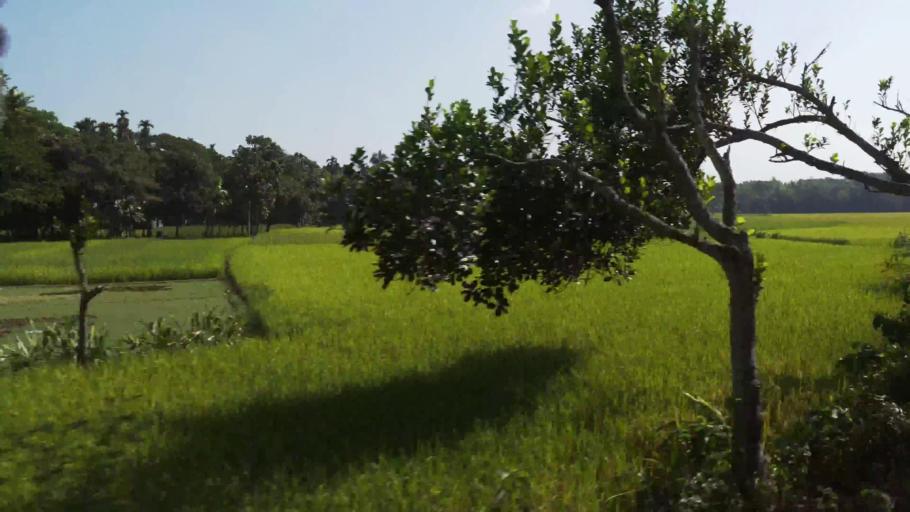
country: BD
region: Dhaka
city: Gafargaon
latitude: 24.5133
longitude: 90.5130
